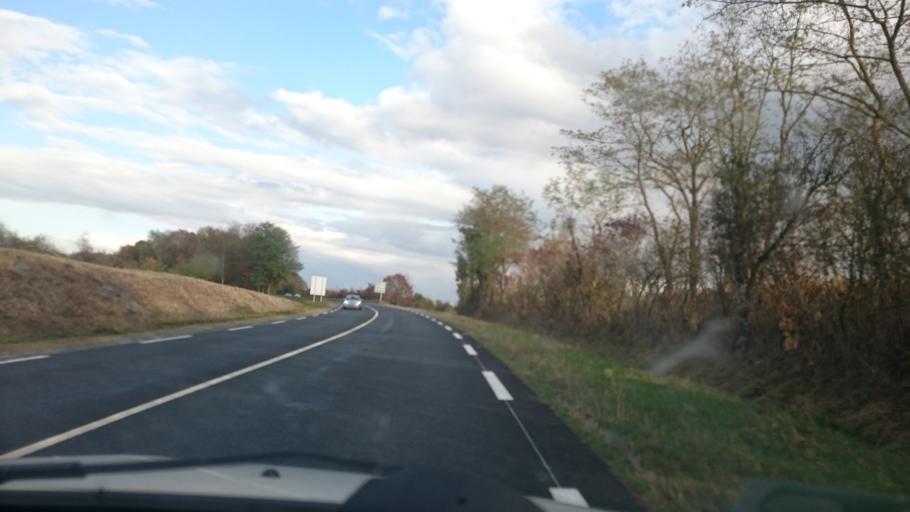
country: FR
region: Centre
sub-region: Departement de l'Indre
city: Saint-Marcel
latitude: 46.6071
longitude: 1.5130
